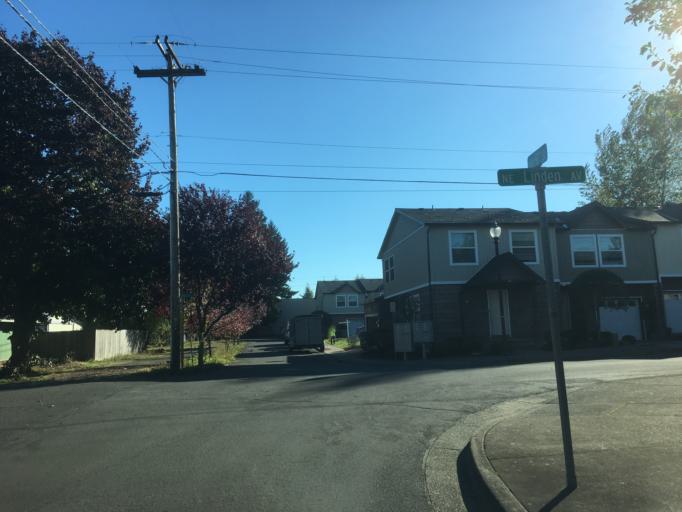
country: US
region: Oregon
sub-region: Multnomah County
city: Gresham
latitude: 45.5037
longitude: -122.4239
